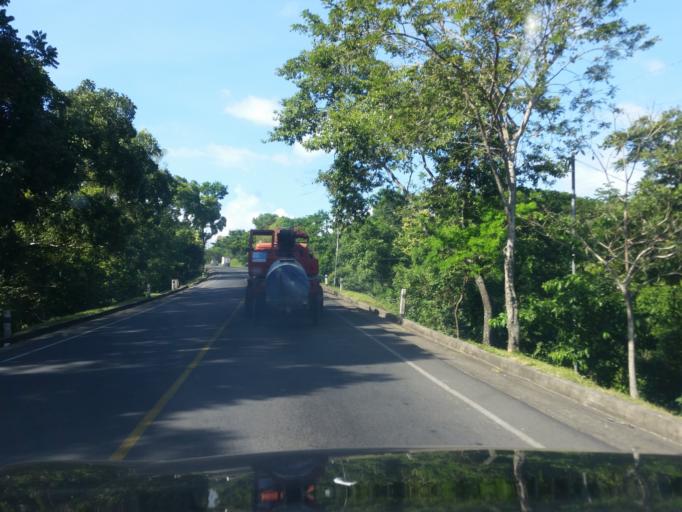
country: NI
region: Masaya
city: San Juan de Oriente
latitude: 11.8964
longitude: -86.0643
